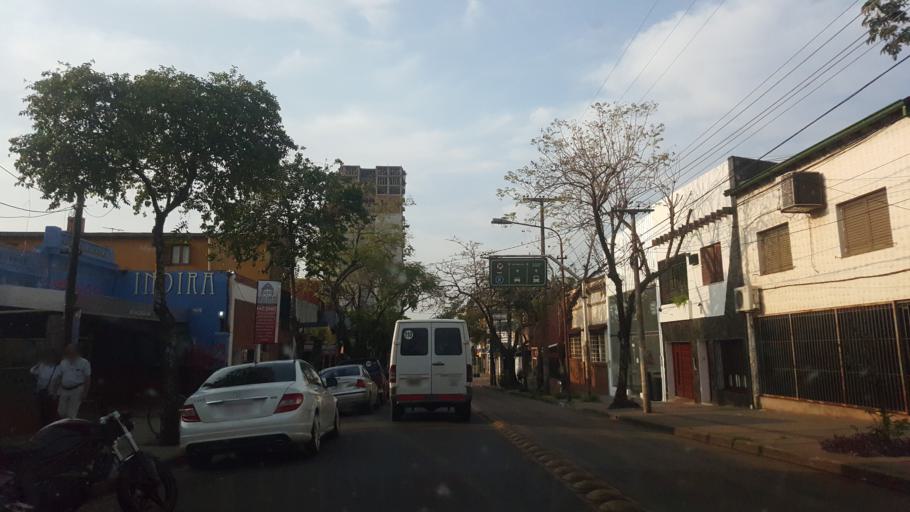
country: AR
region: Misiones
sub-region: Departamento de Capital
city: Posadas
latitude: -27.3646
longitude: -55.8965
